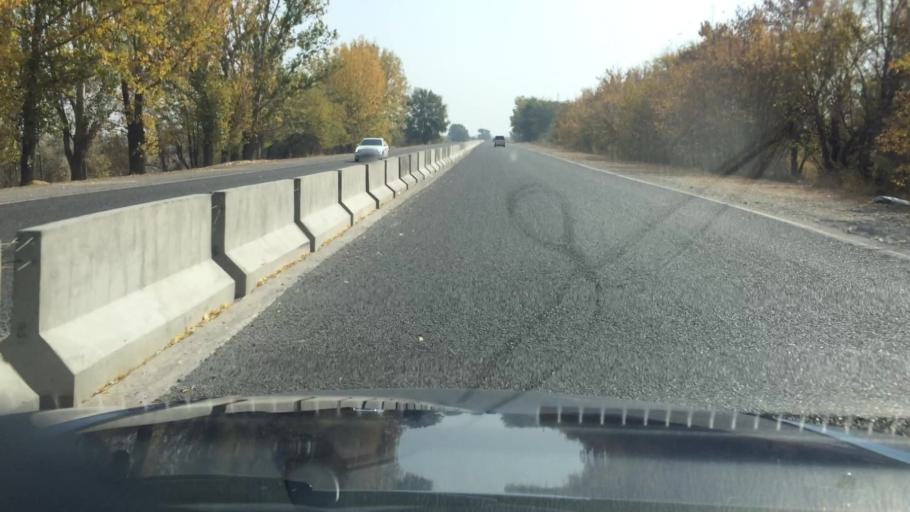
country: KG
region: Chuy
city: Kant
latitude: 42.9633
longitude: 74.9165
